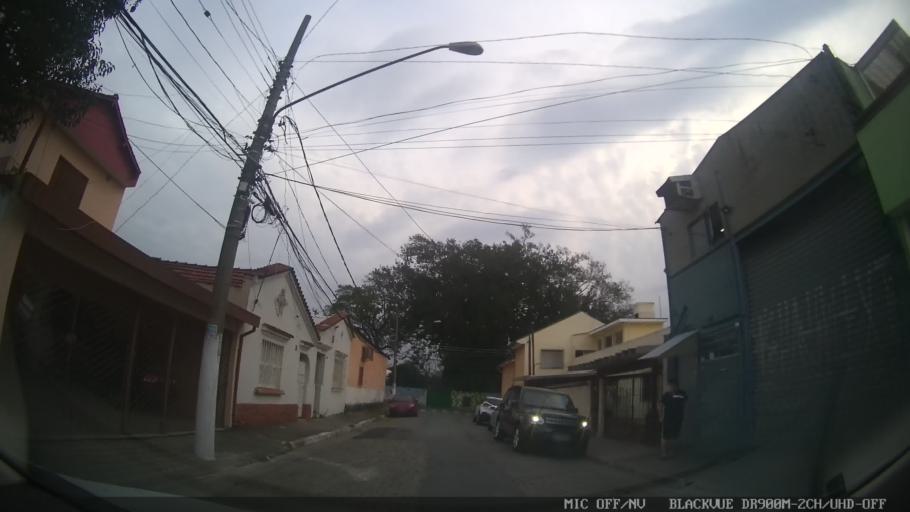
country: BR
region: Sao Paulo
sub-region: Sao Caetano Do Sul
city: Sao Caetano do Sul
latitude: -23.5985
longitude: -46.5901
